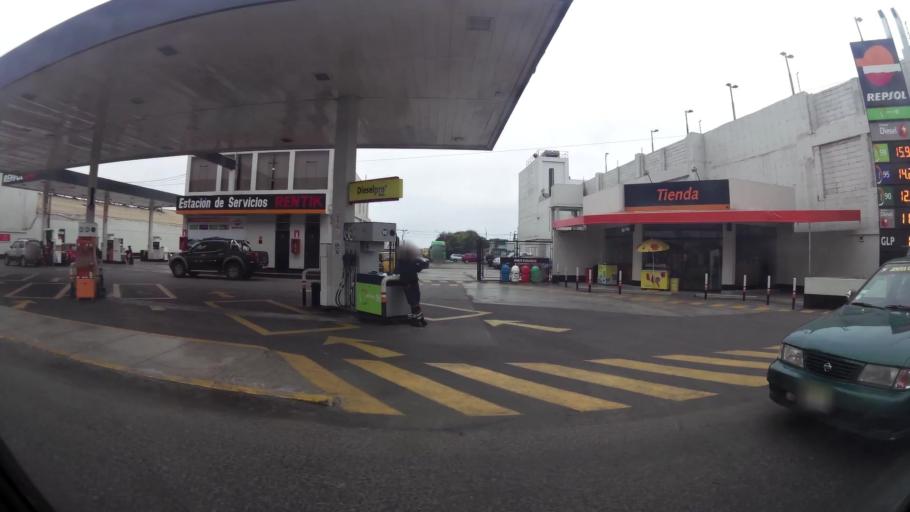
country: PE
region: Ancash
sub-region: Provincia de Santa
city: Chimbote
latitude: -9.0782
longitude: -78.5884
